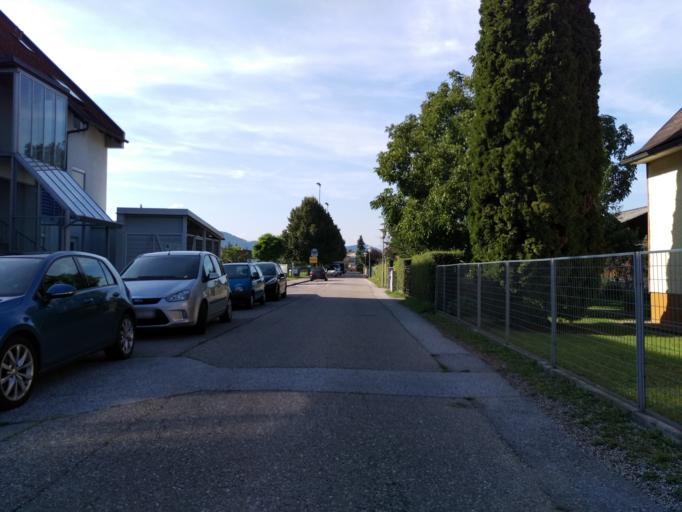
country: AT
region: Styria
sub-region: Politischer Bezirk Graz-Umgebung
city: Seiersberg
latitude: 47.0136
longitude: 15.4188
